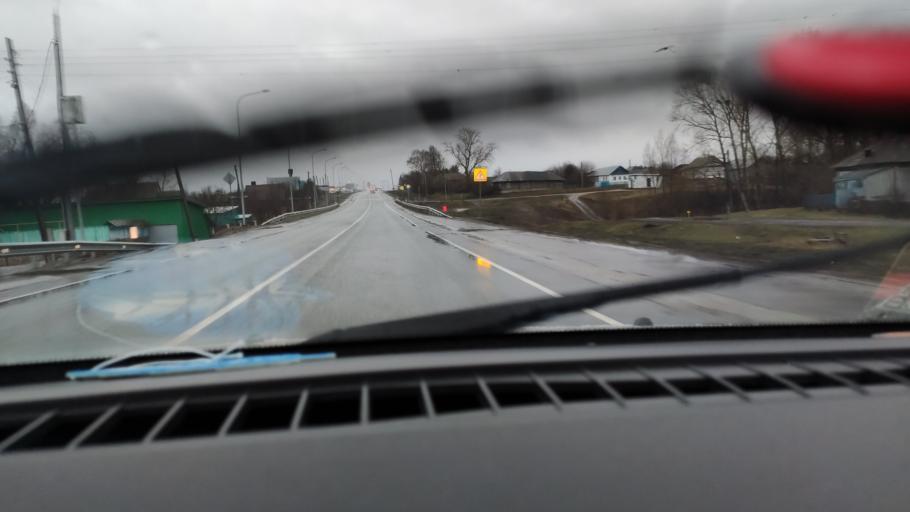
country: RU
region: Tatarstan
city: Mendeleyevsk
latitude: 56.0295
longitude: 52.3740
